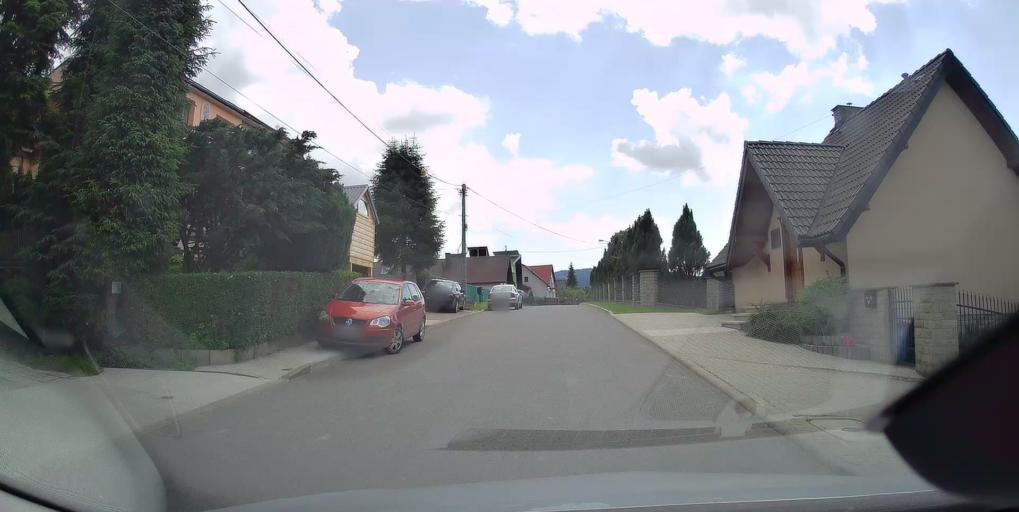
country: PL
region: Lesser Poland Voivodeship
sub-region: Powiat nowosadecki
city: Krynica-Zdroj
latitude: 49.3879
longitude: 20.9541
